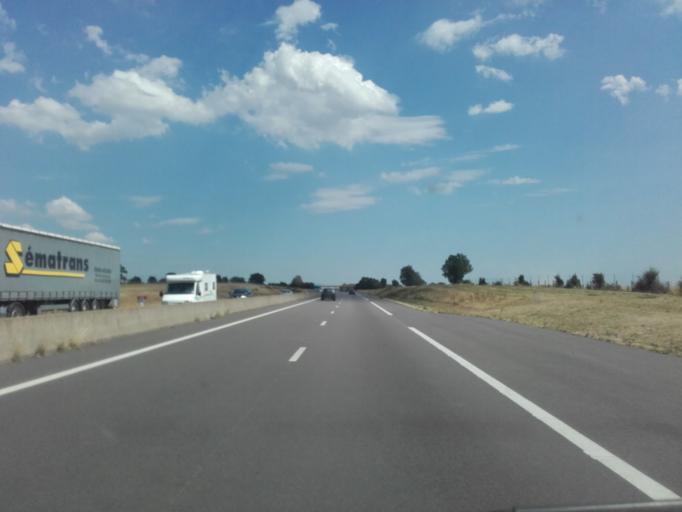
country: FR
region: Bourgogne
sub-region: Departement de la Cote-d'Or
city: Semur-en-Auxois
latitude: 47.4768
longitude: 4.1968
